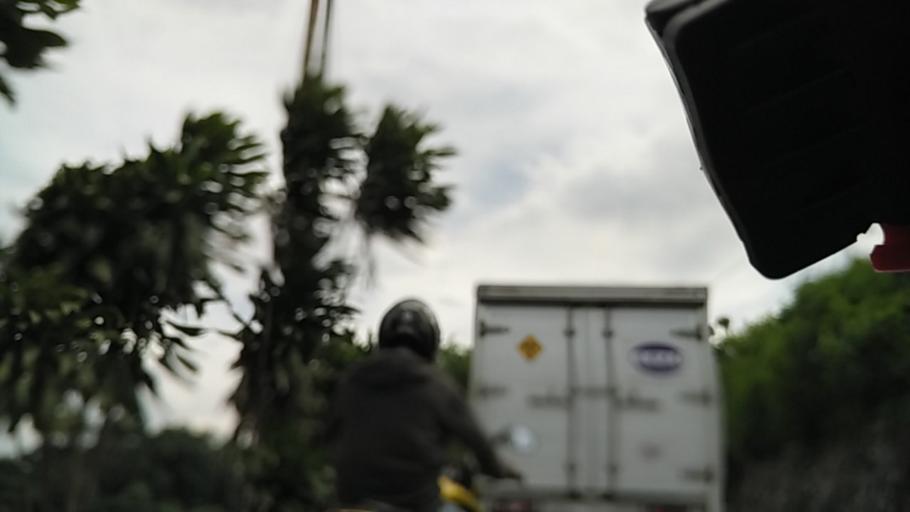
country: ID
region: Central Java
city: Semarang
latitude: -6.9980
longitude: 110.4111
